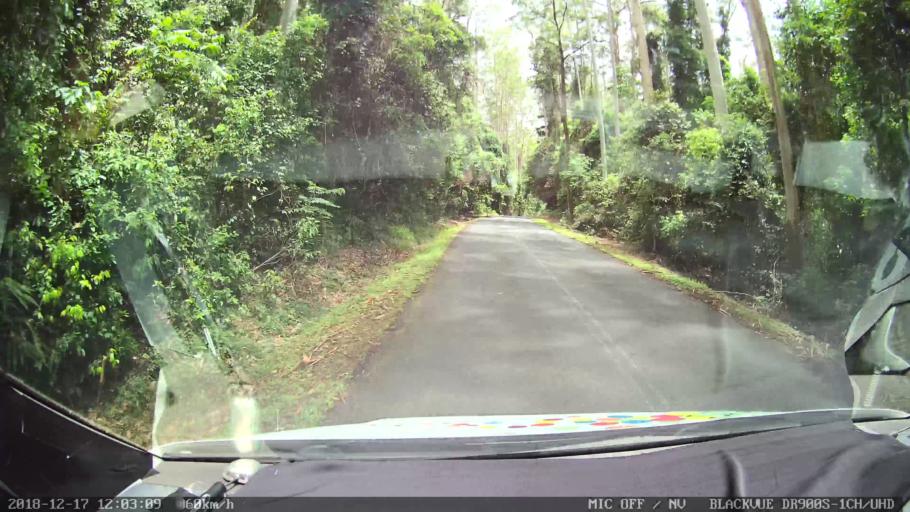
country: AU
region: New South Wales
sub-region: Kyogle
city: Kyogle
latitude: -28.5107
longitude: 152.5688
